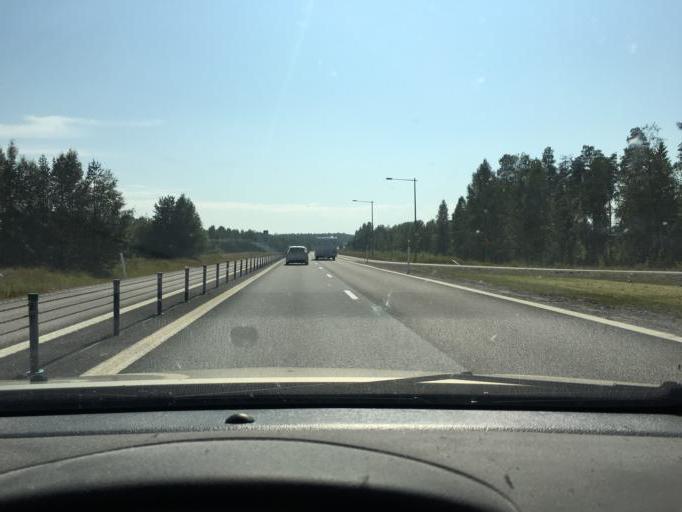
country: SE
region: Norrbotten
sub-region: Lulea Kommun
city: Gammelstad
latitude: 65.6146
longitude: 22.0563
